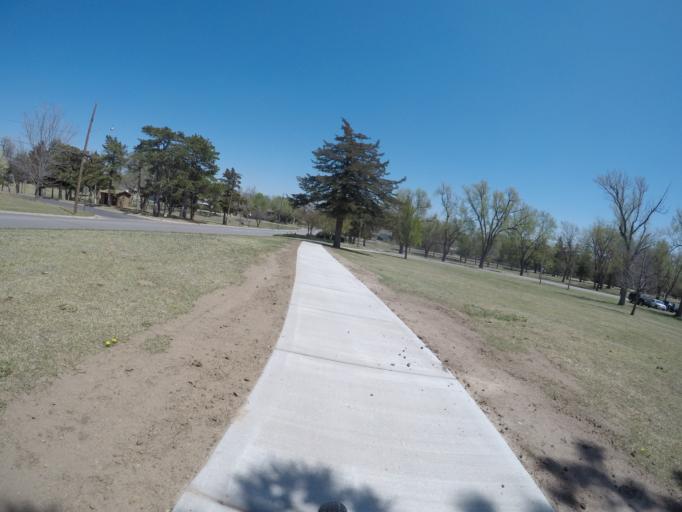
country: US
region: Kansas
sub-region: Pratt County
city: Pratt
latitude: 37.6406
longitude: -98.7320
